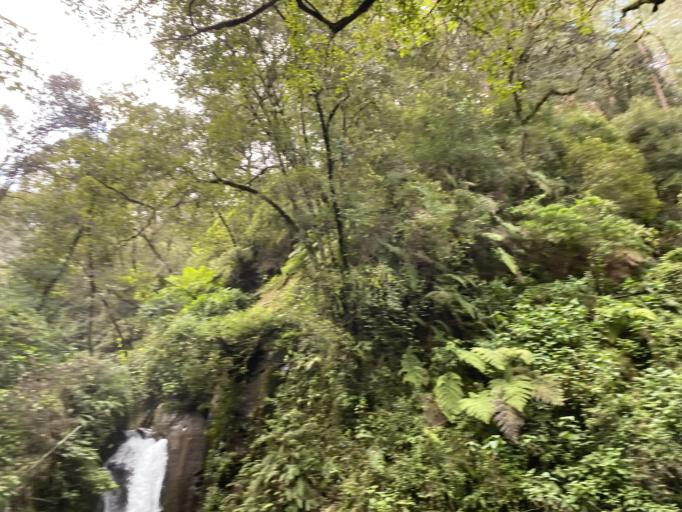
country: MX
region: Veracruz
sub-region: Altotonga
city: Adolfo Moreno
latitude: 19.7380
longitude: -97.2523
